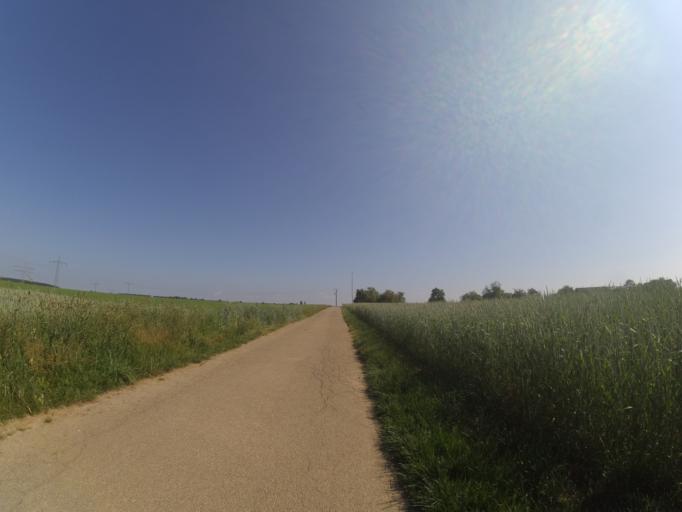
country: DE
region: Baden-Wuerttemberg
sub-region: Tuebingen Region
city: Beimerstetten
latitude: 48.4677
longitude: 9.9887
